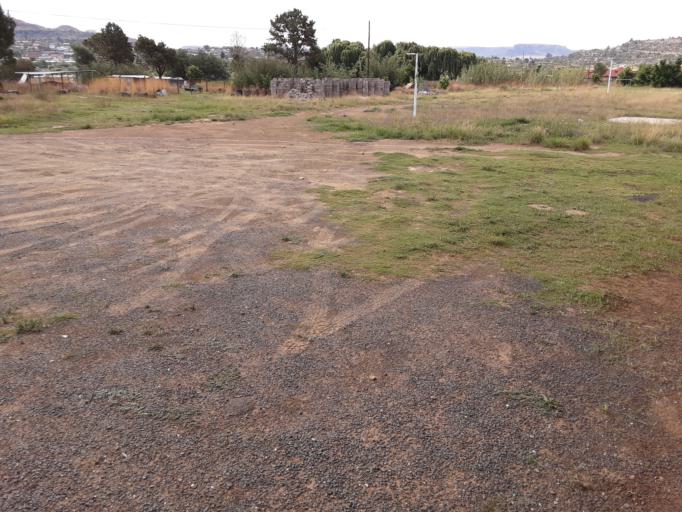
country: LS
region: Maseru
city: Maseru
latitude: -29.3457
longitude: 27.5211
